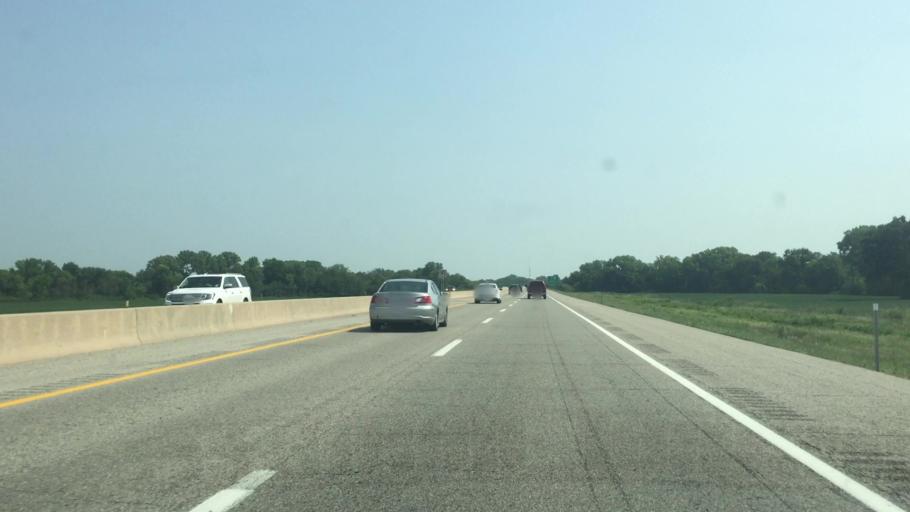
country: US
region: Kansas
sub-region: Lyon County
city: Emporia
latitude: 38.3822
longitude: -96.2634
